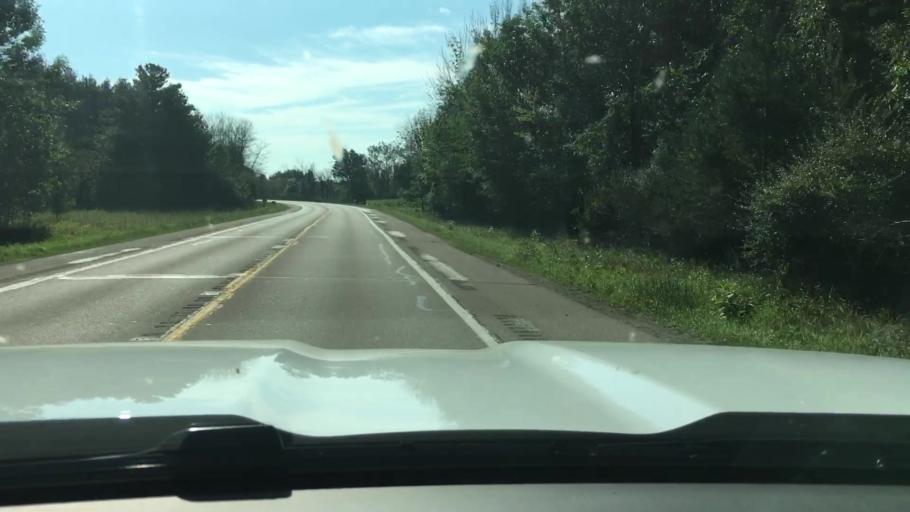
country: US
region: Michigan
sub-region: Montcalm County
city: Edmore
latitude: 43.4106
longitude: -85.1199
